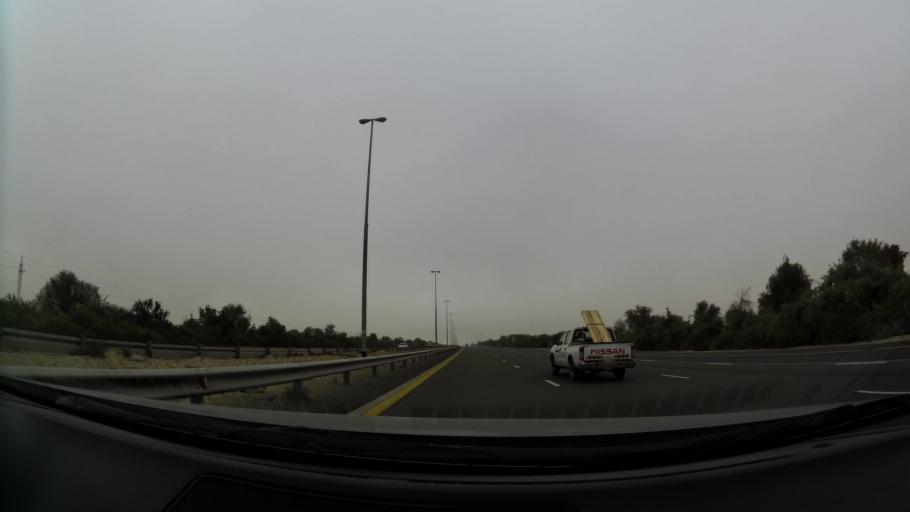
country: AE
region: Dubai
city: Dubai
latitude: 25.0576
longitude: 55.4185
